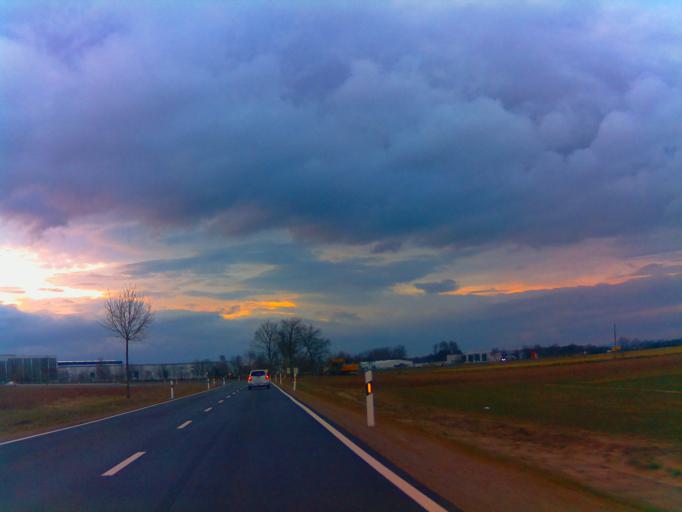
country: DE
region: Hesse
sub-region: Regierungsbezirk Darmstadt
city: Gross-Rohrheim
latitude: 49.7141
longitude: 8.4996
